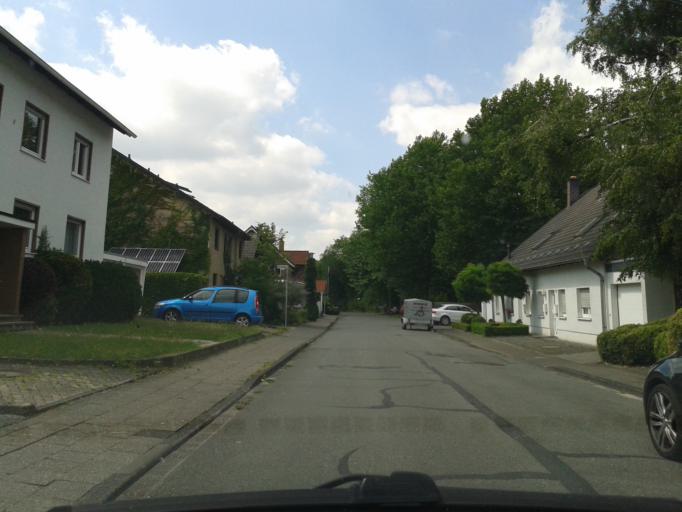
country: DE
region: North Rhine-Westphalia
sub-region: Regierungsbezirk Detmold
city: Paderborn
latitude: 51.7352
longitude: 8.7378
